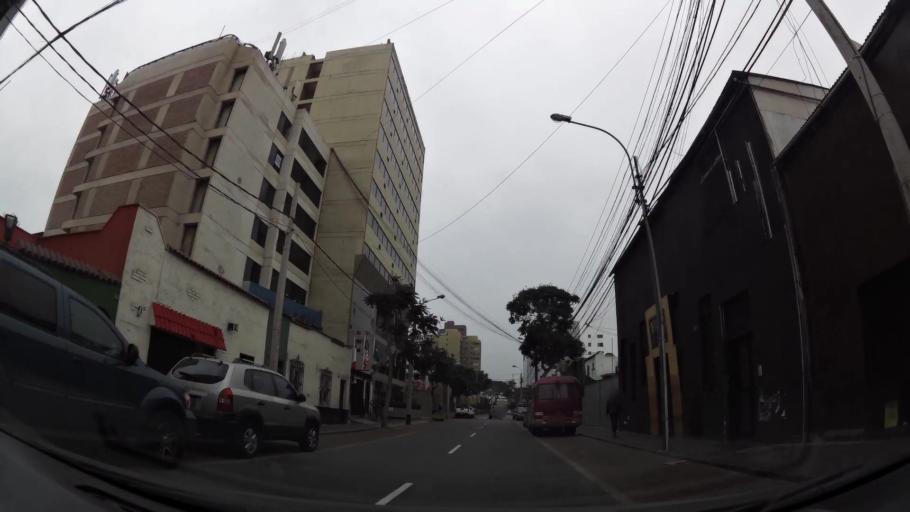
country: PE
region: Lima
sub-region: Lima
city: San Isidro
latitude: -12.1213
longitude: -77.0320
